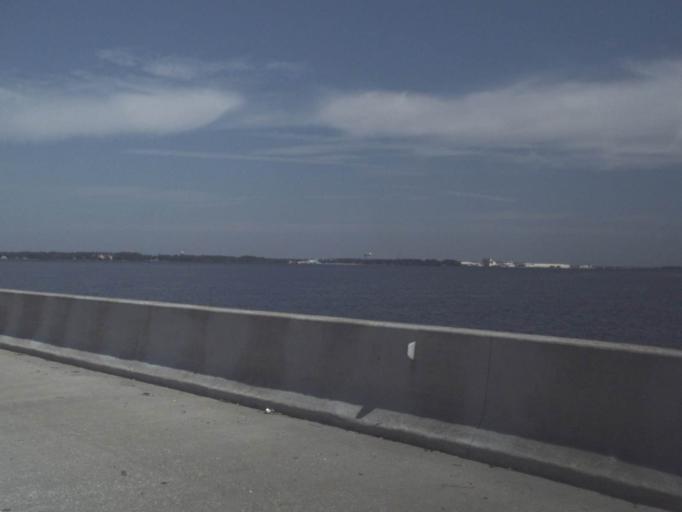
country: US
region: Florida
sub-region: Clay County
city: Orange Park
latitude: 30.1887
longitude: -81.6467
